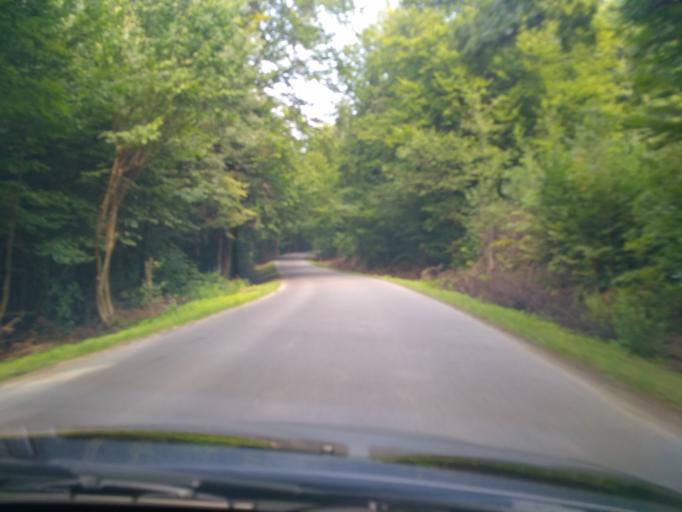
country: PL
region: Subcarpathian Voivodeship
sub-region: Powiat strzyzowski
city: Czudec
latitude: 49.9679
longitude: 21.8396
